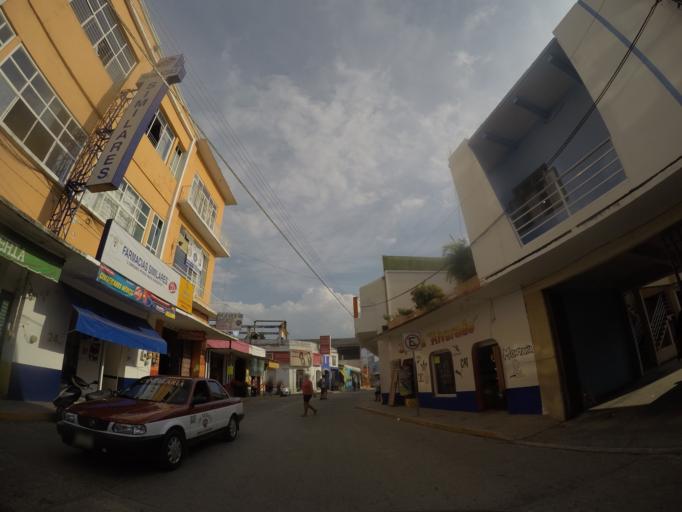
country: MX
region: Oaxaca
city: San Pedro Pochutla
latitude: 15.7456
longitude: -96.4666
